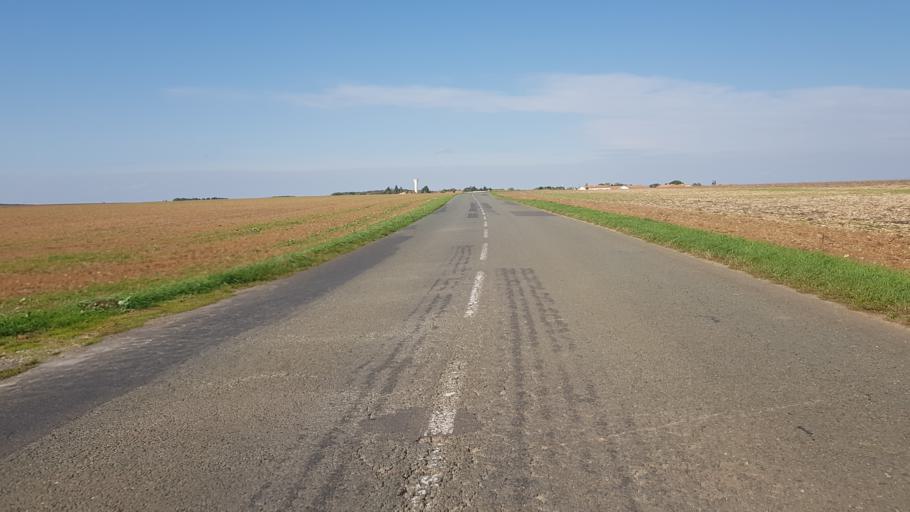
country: FR
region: Poitou-Charentes
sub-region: Departement de la Vienne
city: Chasseneuil-du-Poitou
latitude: 46.6530
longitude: 0.3428
